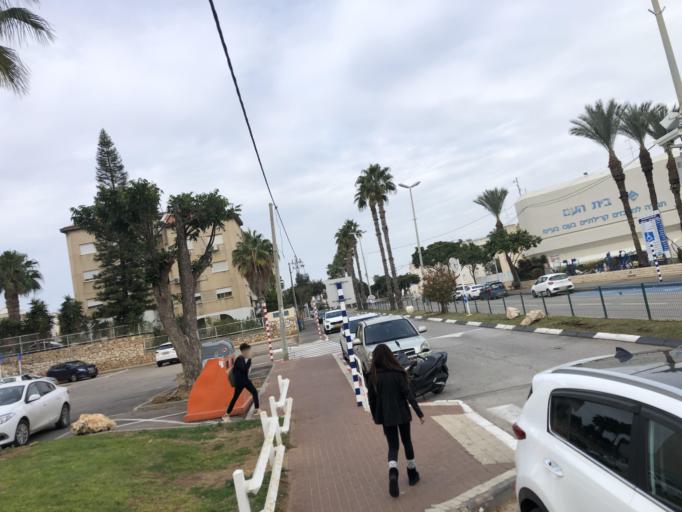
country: IL
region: Northern District
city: `Akko
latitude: 32.9305
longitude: 35.0923
